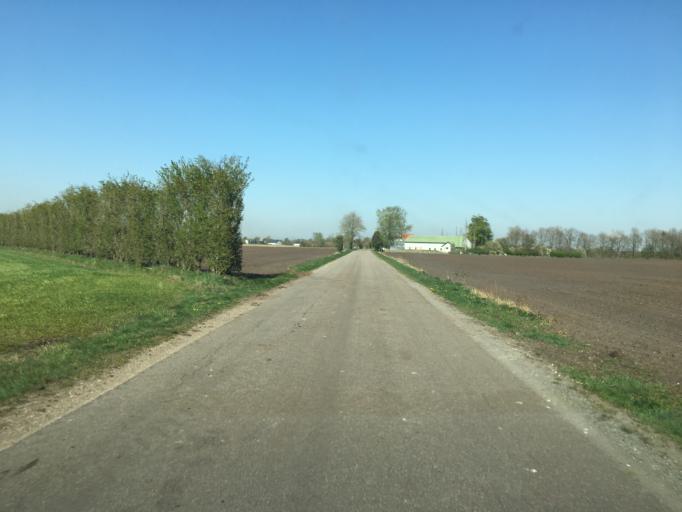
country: DK
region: South Denmark
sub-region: Aabenraa Kommune
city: Rodekro
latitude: 55.0829
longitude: 9.2652
